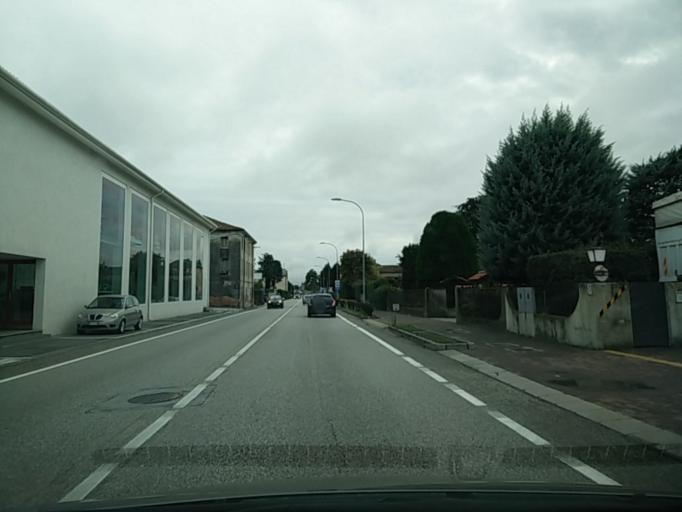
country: IT
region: Veneto
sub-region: Provincia di Padova
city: Cittadella
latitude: 45.6627
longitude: 11.7800
